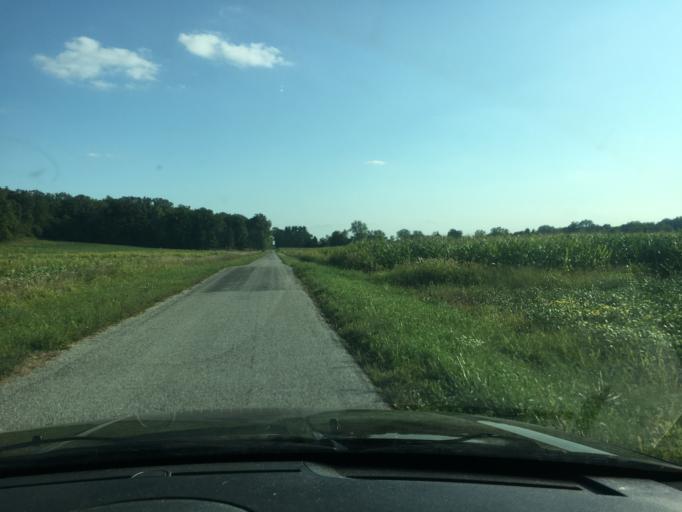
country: US
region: Ohio
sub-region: Logan County
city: West Liberty
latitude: 40.2422
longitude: -83.7857
